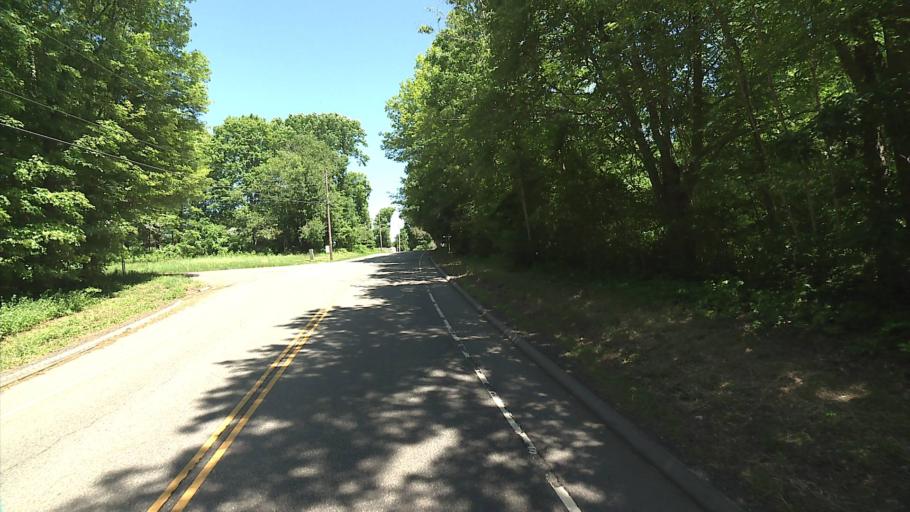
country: US
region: Rhode Island
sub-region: Washington County
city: Hopkinton
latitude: 41.5043
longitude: -71.8387
